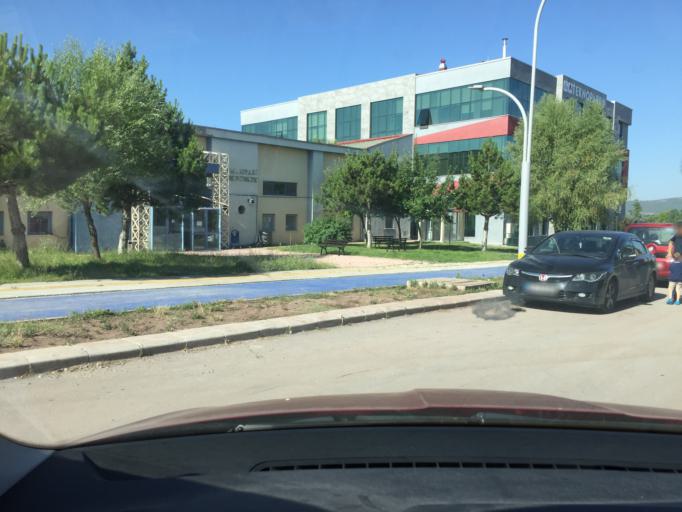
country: TR
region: Eskisehir
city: Eskisehir
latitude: 39.7472
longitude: 30.4748
